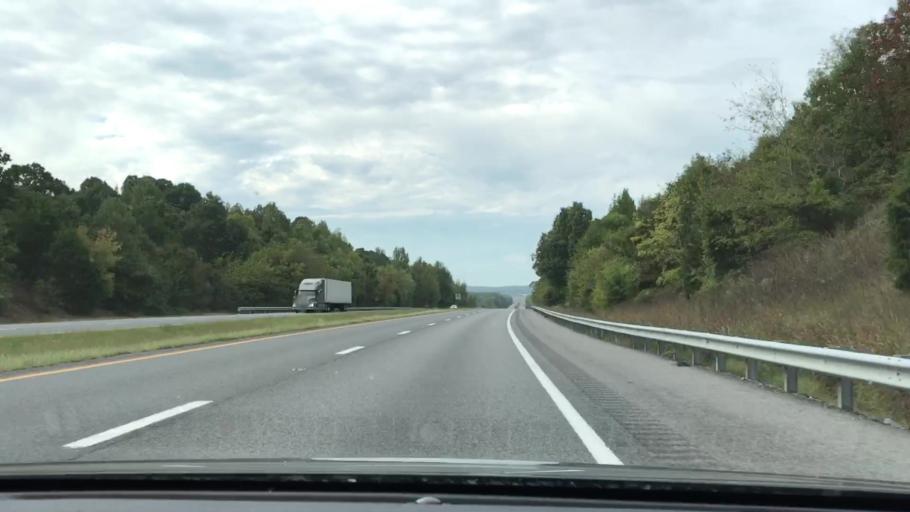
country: US
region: Kentucky
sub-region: Marshall County
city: Benton
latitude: 36.8948
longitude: -88.3492
